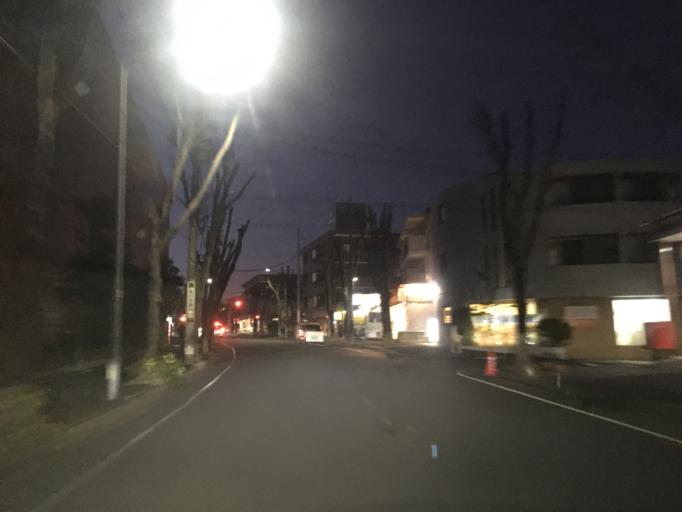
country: JP
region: Tokyo
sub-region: Machida-shi
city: Machida
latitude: 35.5502
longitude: 139.5252
